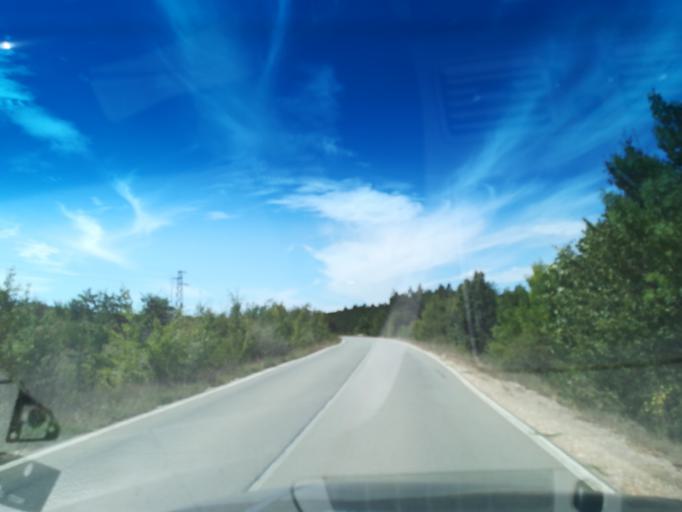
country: BG
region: Plovdiv
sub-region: Obshtina Suedinenie
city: Suedinenie
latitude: 42.3998
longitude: 24.5438
